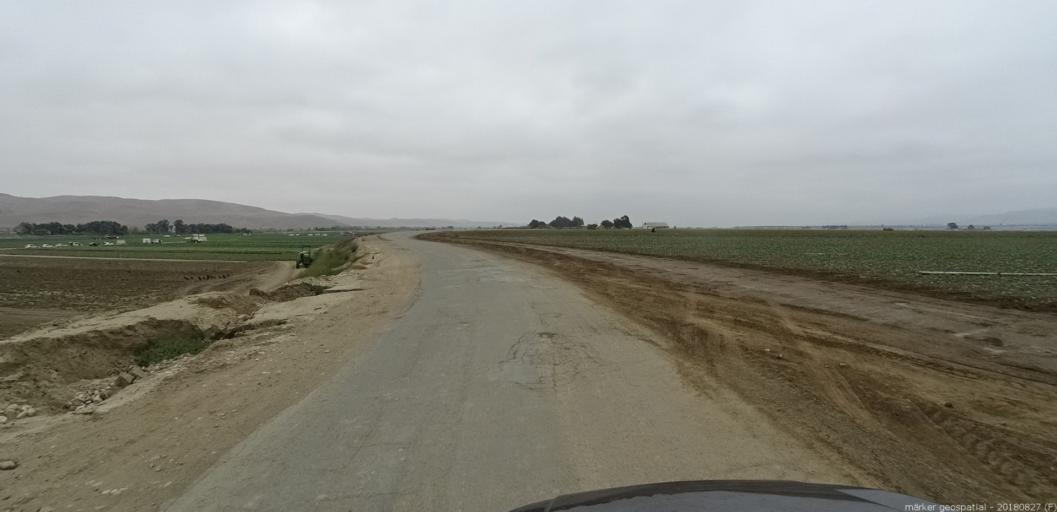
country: US
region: California
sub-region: Monterey County
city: Greenfield
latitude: 36.3300
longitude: -121.2095
